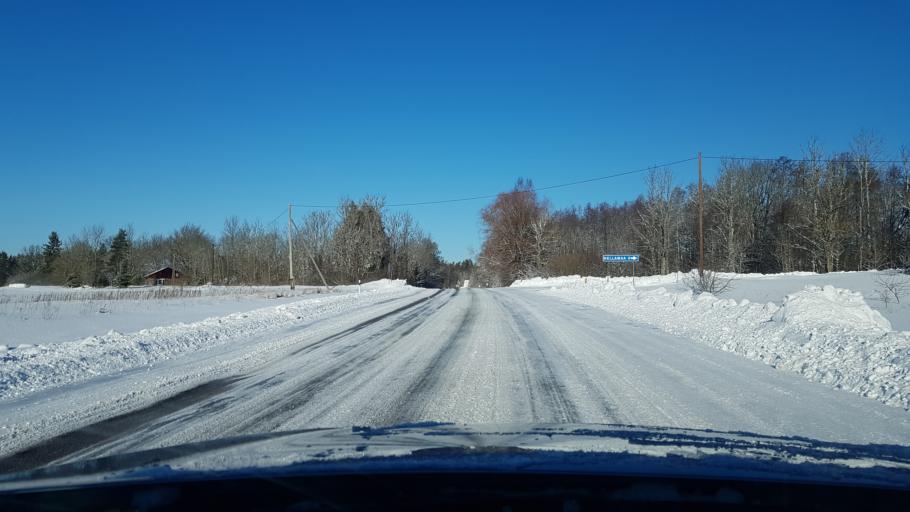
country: EE
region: Hiiumaa
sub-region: Kaerdla linn
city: Kardla
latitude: 58.9175
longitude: 22.7945
